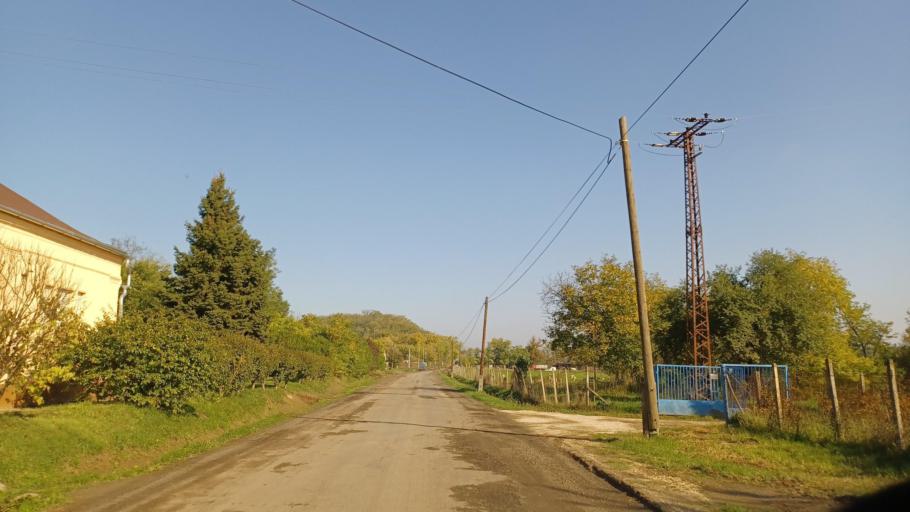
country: HU
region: Tolna
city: Szedres
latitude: 46.5165
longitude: 18.5909
